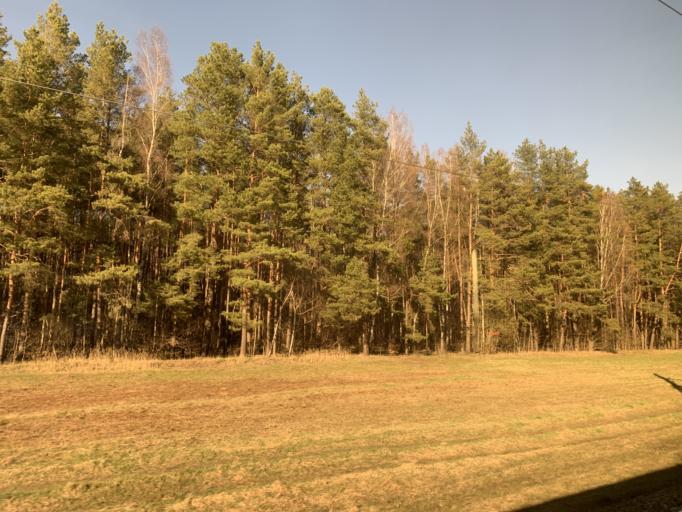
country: BY
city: Soly
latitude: 54.4919
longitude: 26.2902
